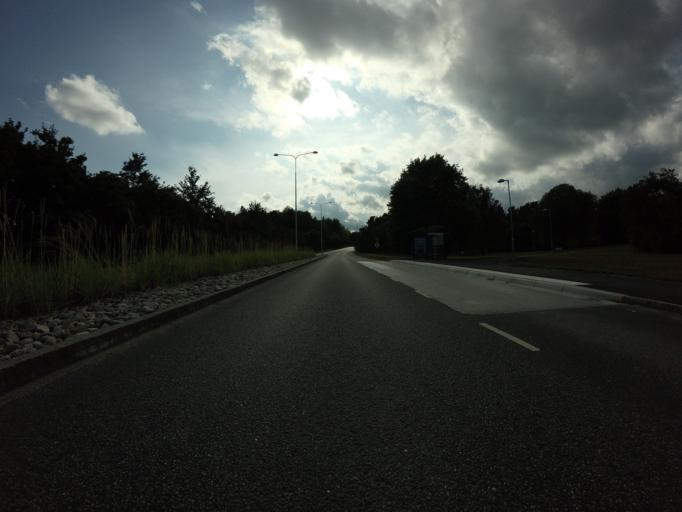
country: SE
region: Stockholm
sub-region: Lidingo
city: Lidingoe
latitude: 59.3717
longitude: 18.1546
